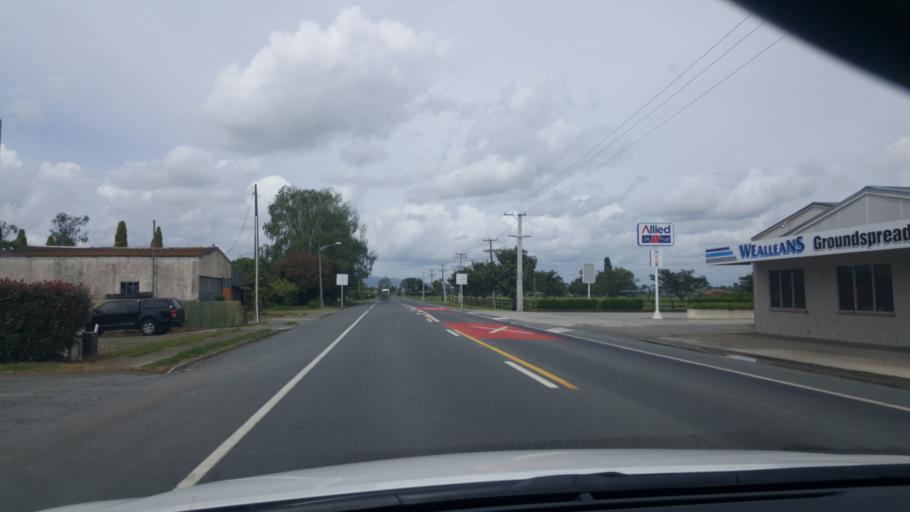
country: NZ
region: Waikato
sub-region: Matamata-Piako District
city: Matamata
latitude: -37.8831
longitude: 175.7618
